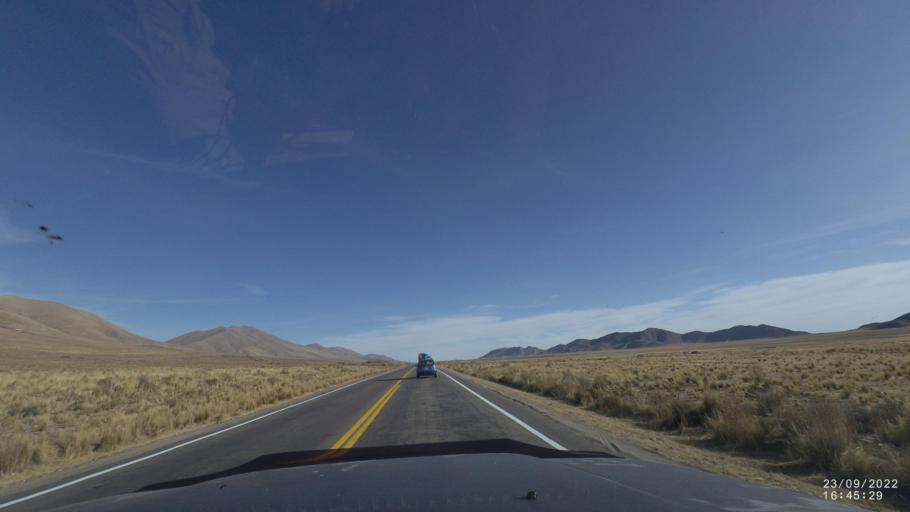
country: BO
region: Oruro
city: Poopo
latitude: -18.3425
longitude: -66.9861
